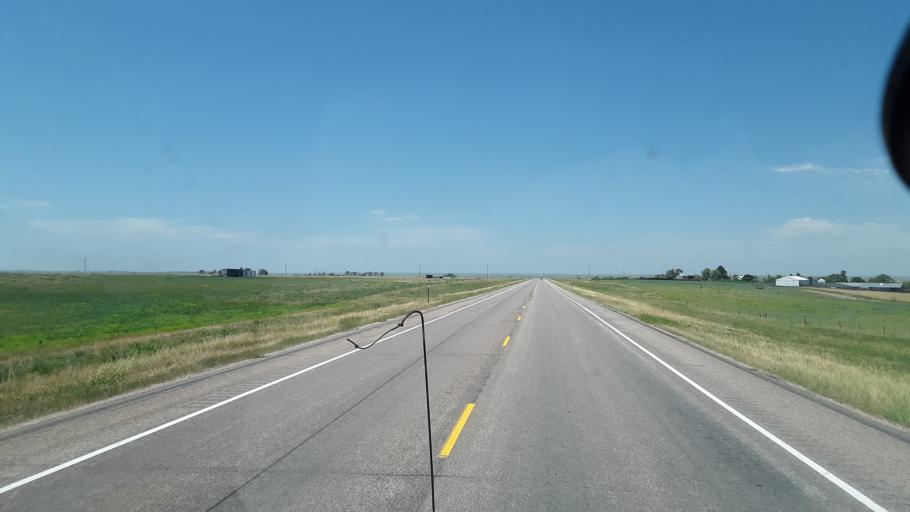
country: US
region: South Dakota
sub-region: Pennington County
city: Box Elder
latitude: 43.8590
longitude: -102.6126
